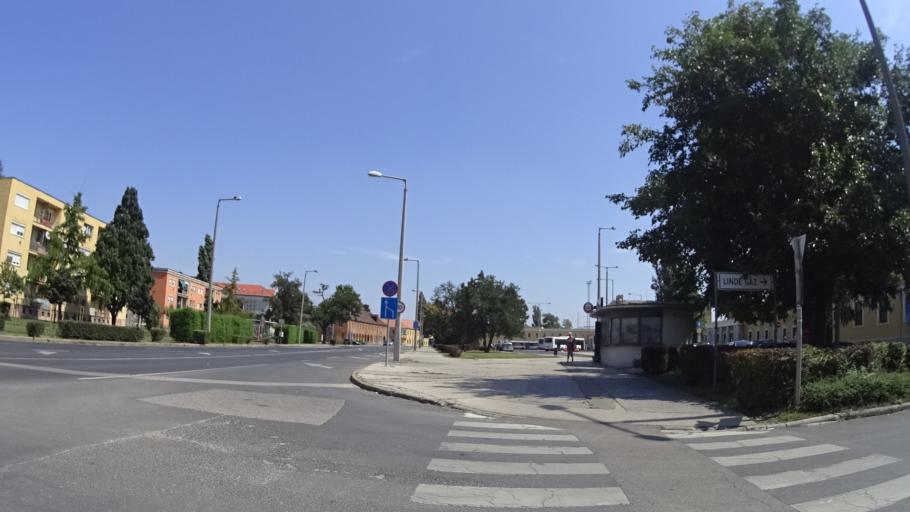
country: HU
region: Fejer
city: Szekesfehervar
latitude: 47.1834
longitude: 18.4226
